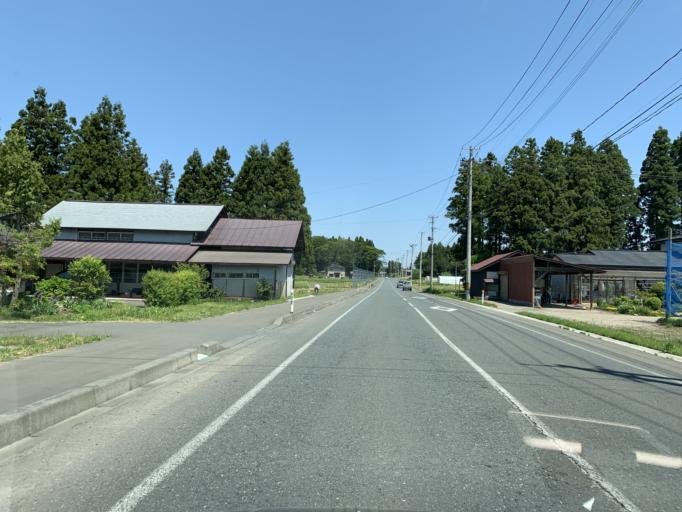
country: JP
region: Iwate
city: Kitakami
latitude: 39.2377
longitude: 141.0666
